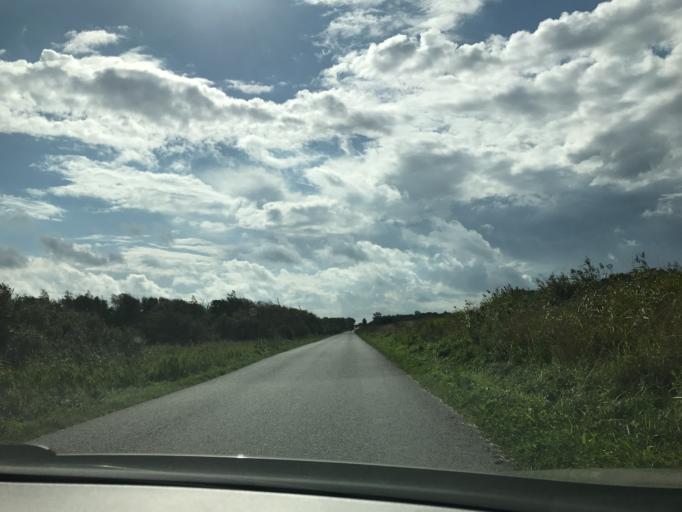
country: DK
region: South Denmark
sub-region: Middelfart Kommune
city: Norre Aby
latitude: 55.4211
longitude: 9.8291
